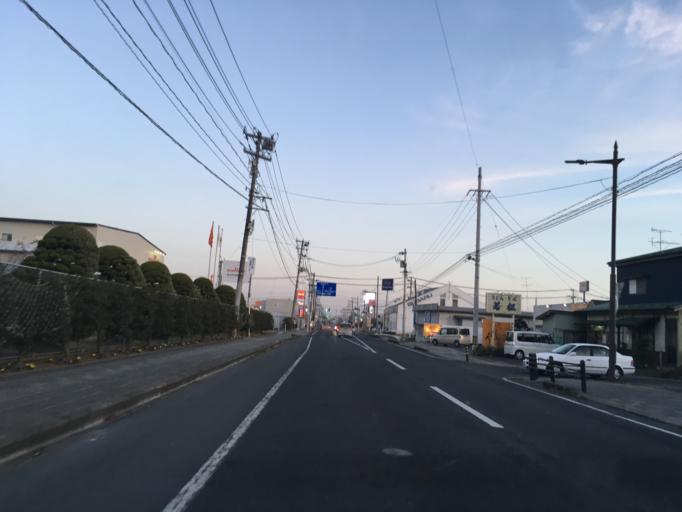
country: JP
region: Miyagi
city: Wakuya
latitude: 38.6879
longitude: 141.1862
